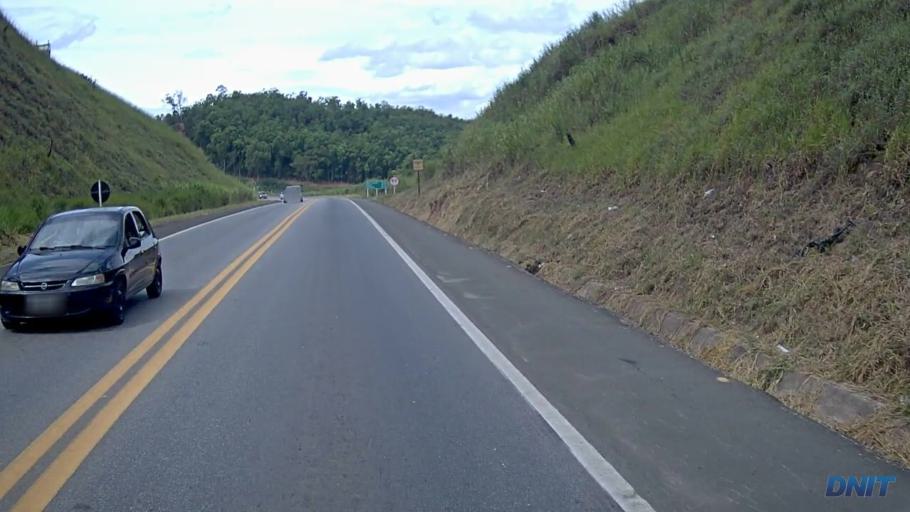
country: BR
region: Minas Gerais
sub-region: Ipatinga
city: Ipatinga
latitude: -19.4498
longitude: -42.5167
